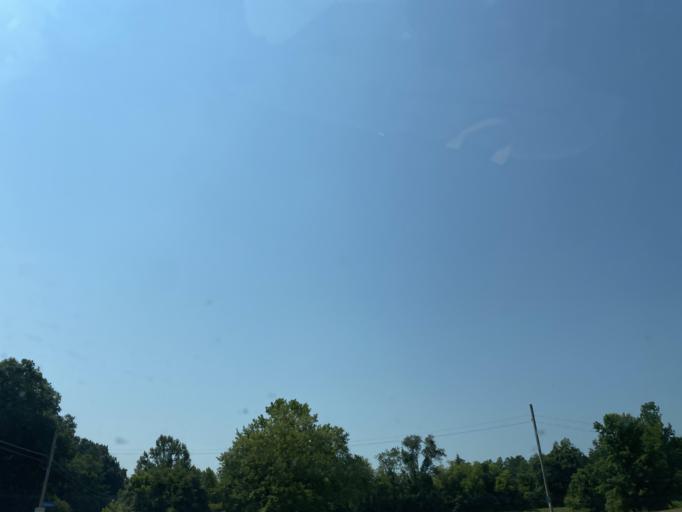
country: US
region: Kentucky
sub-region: Campbell County
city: Claryville
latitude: 38.8350
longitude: -84.4574
